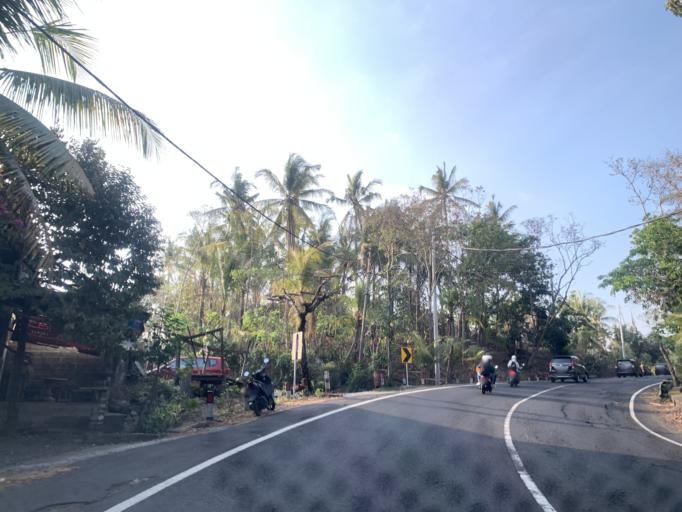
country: ID
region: Bali
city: Banjar Delodrurung
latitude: -8.5005
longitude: 115.0208
